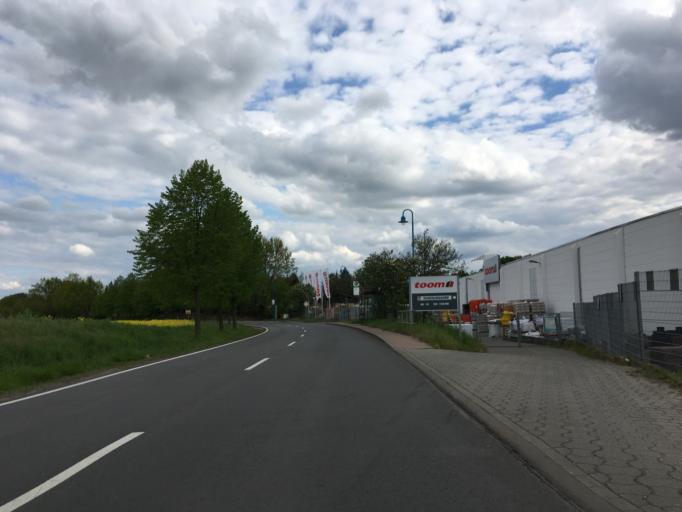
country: DE
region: Brandenburg
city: Bernau bei Berlin
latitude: 52.6674
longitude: 13.5835
